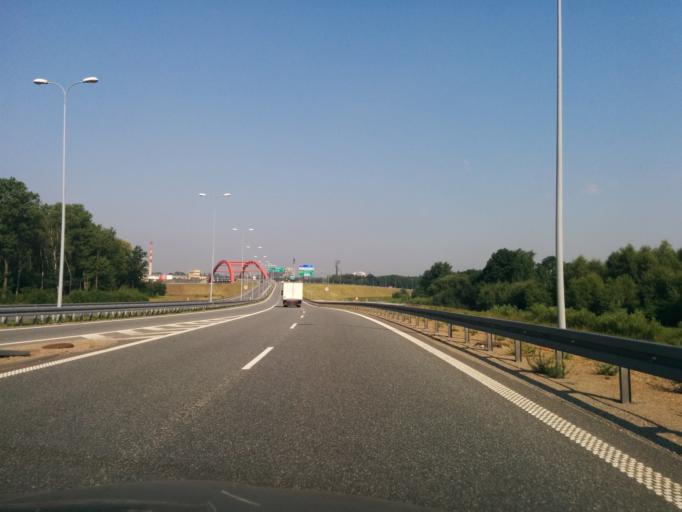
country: PL
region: Silesian Voivodeship
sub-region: Powiat gliwicki
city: Przyszowice
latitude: 50.2668
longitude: 18.7362
